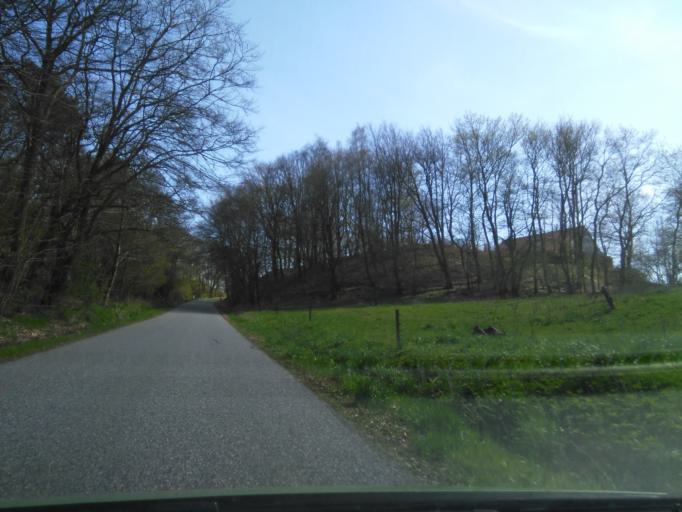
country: DK
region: Central Jutland
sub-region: Viborg Kommune
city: Viborg
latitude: 56.3613
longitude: 9.3385
